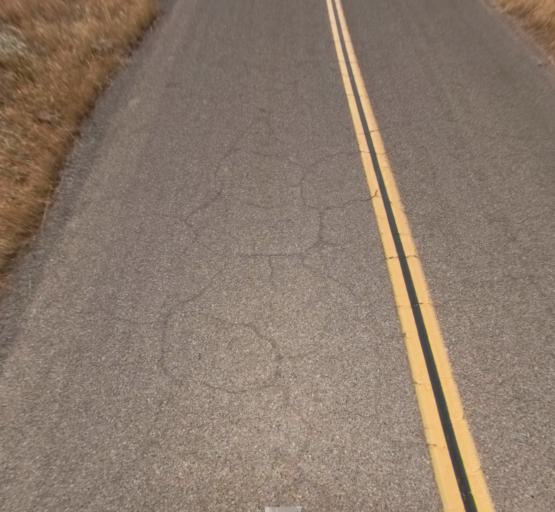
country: US
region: California
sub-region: Madera County
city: Yosemite Lakes
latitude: 37.0289
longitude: -119.7028
